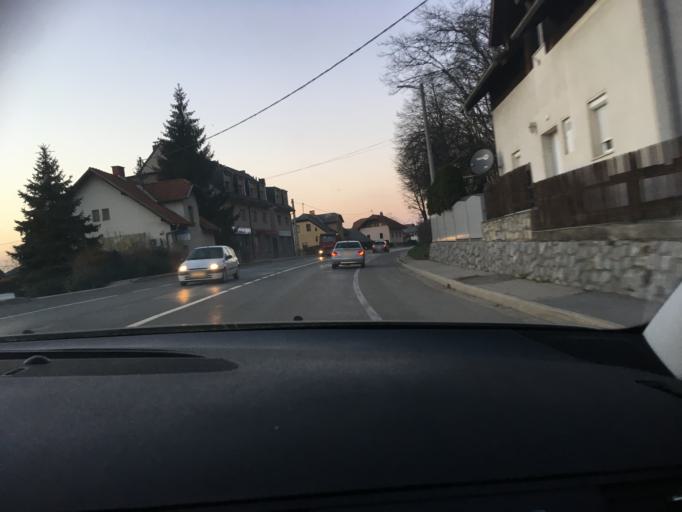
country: SI
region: Skofljica
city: Skofljica
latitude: 45.9877
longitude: 14.5681
